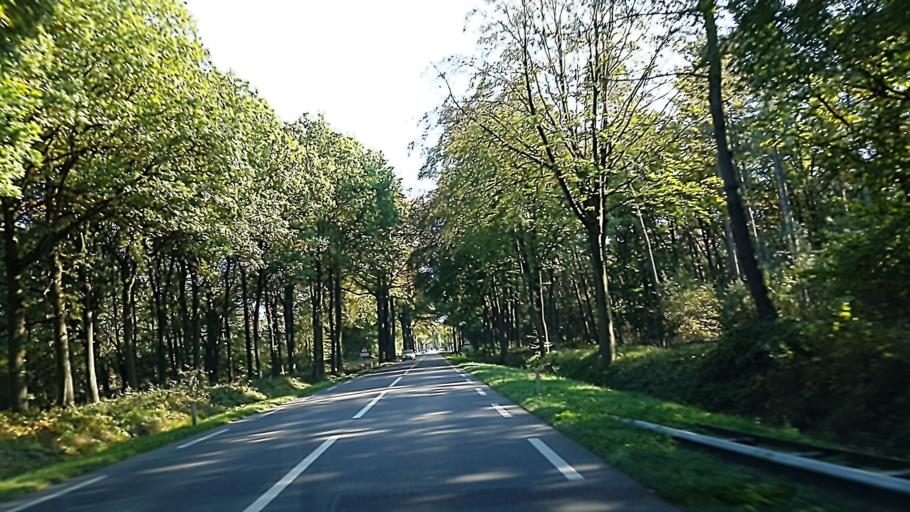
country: BE
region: Flanders
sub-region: Provincie Antwerpen
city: Stabroek
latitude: 51.3900
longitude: 4.3612
